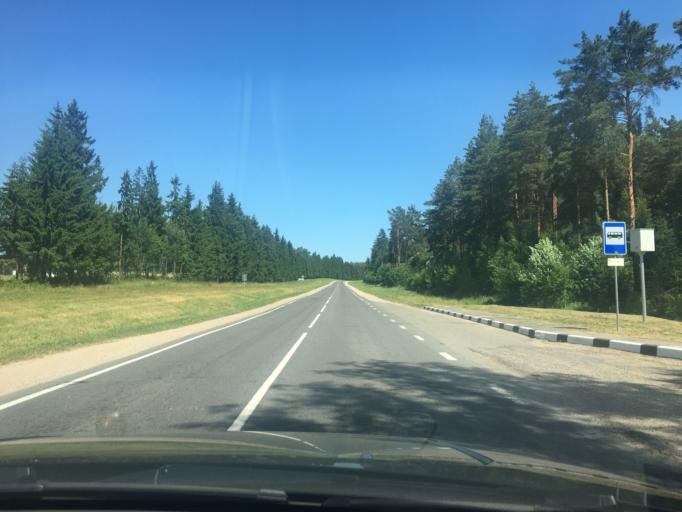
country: BY
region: Grodnenskaya
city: Hal'shany
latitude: 54.2162
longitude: 25.9691
